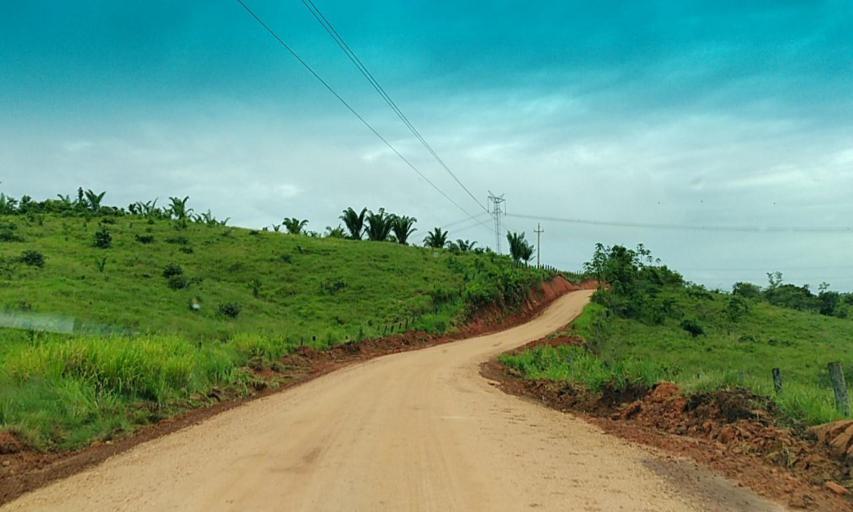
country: BR
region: Para
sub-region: Altamira
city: Altamira
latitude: -3.1038
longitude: -51.6339
